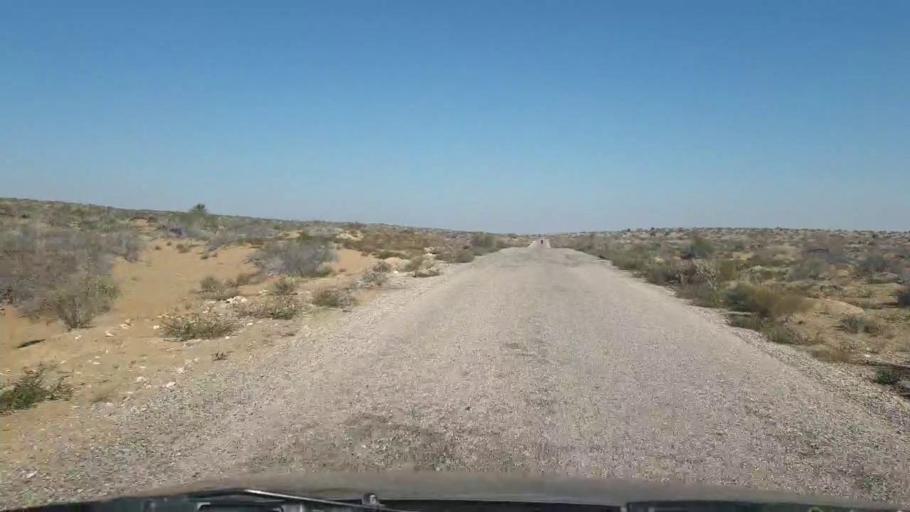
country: PK
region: Sindh
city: Bozdar
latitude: 26.9986
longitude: 68.8600
